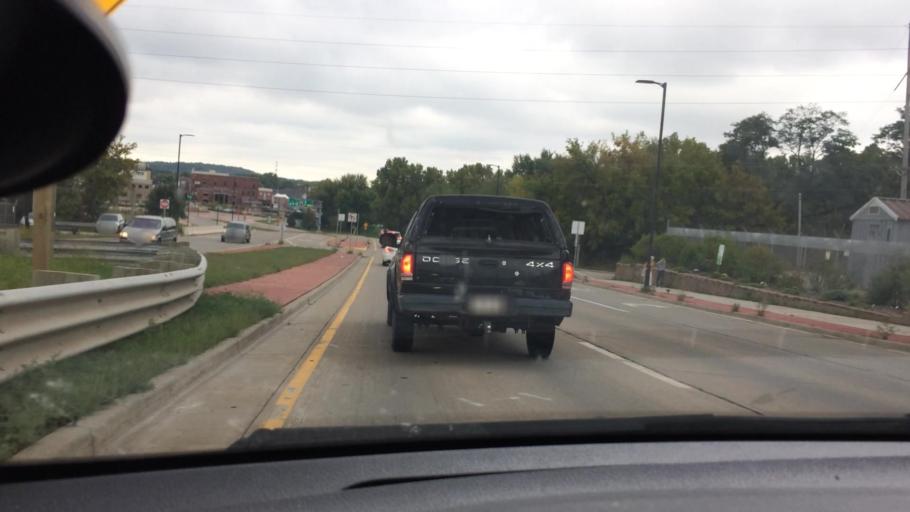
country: US
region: Wisconsin
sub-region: Chippewa County
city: Chippewa Falls
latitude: 44.9324
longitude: -91.3879
